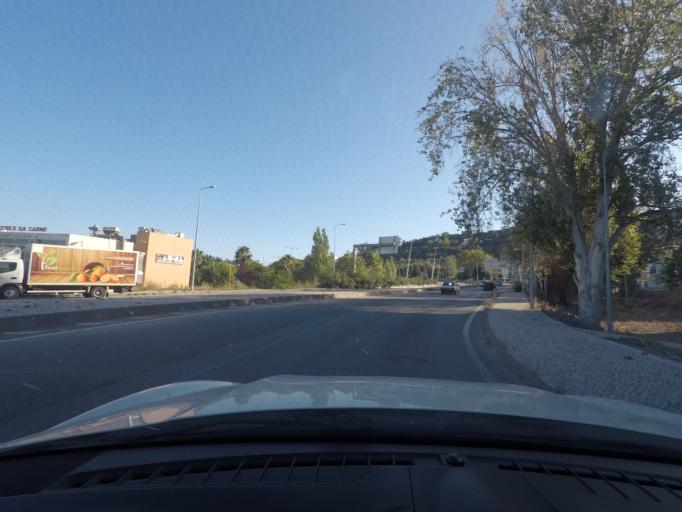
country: PT
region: Coimbra
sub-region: Coimbra
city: Coimbra
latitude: 40.1960
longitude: -8.4316
